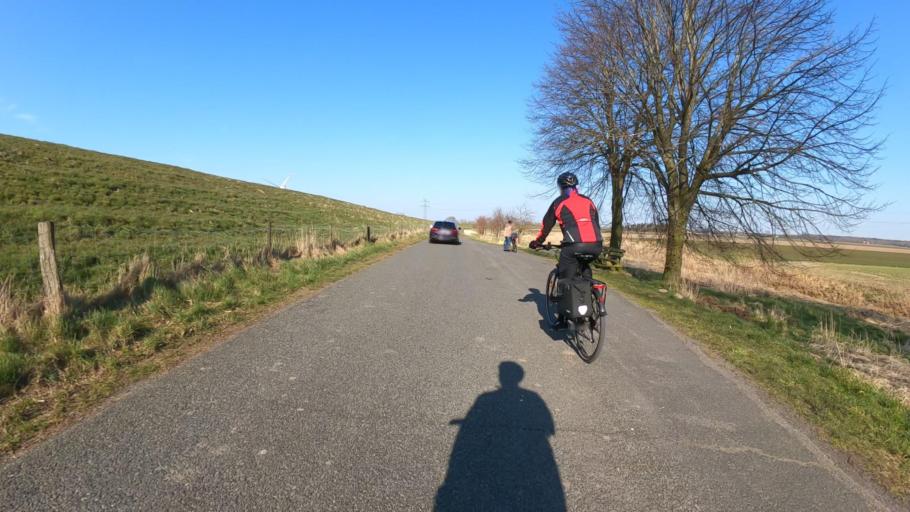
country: DE
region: Schleswig-Holstein
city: Seester
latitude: 53.7316
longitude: 9.6036
